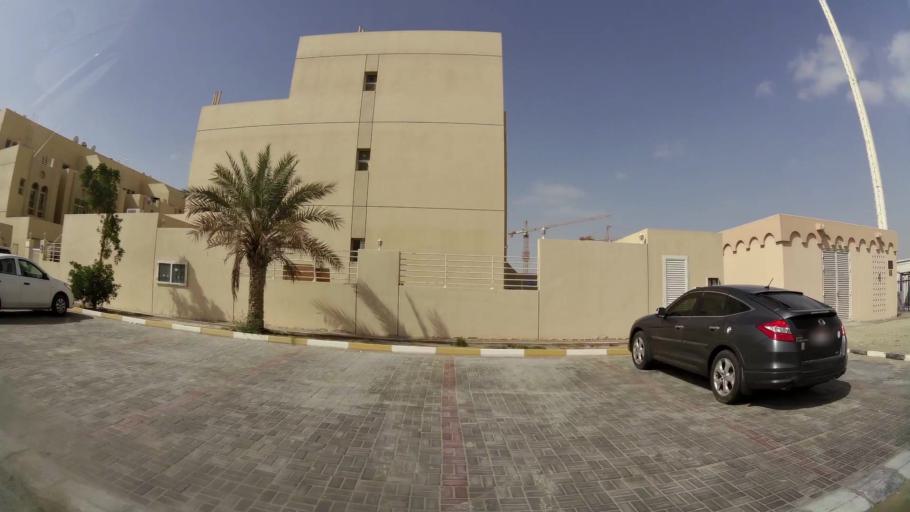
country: AE
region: Abu Dhabi
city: Abu Dhabi
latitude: 24.4280
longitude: 54.5832
